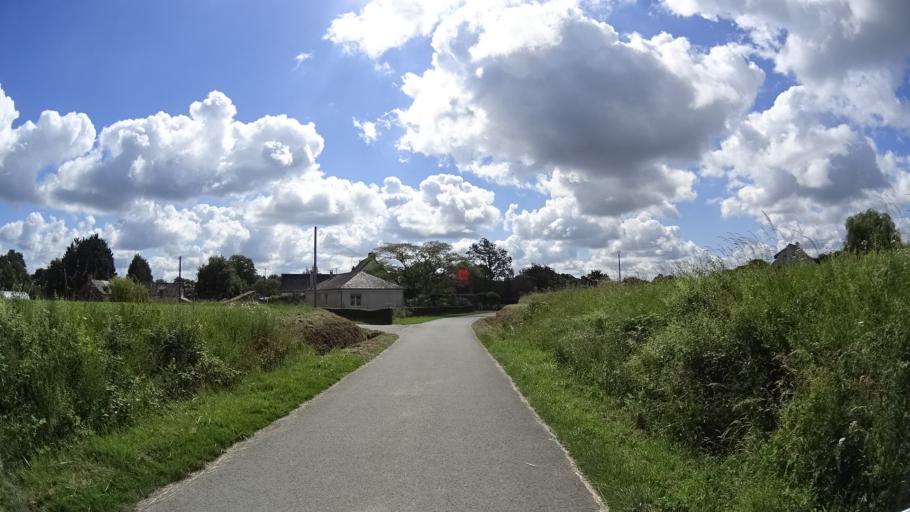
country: FR
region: Brittany
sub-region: Departement d'Ille-et-Vilaine
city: Le Rheu
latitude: 48.1158
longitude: -1.8027
